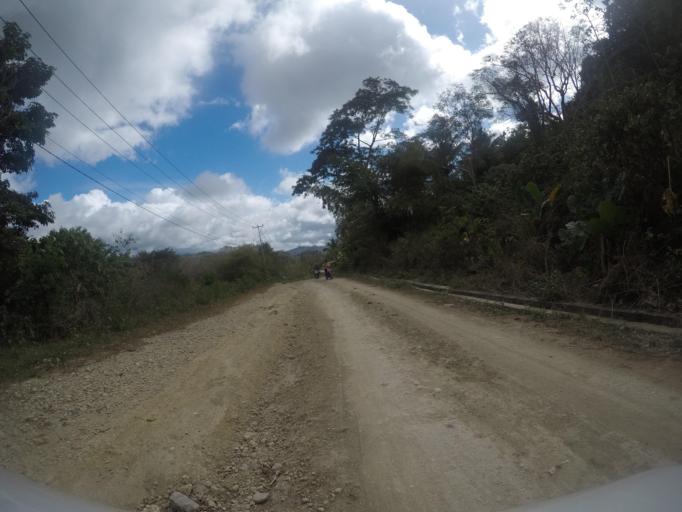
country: TL
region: Lautem
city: Lospalos
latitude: -8.5519
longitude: 126.8986
